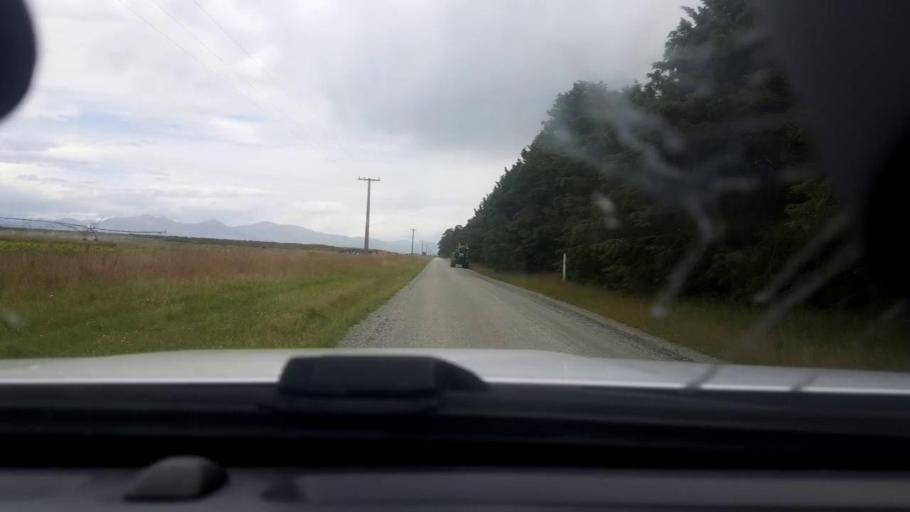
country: NZ
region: Canterbury
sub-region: Timaru District
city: Timaru
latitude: -44.1550
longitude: 171.3986
